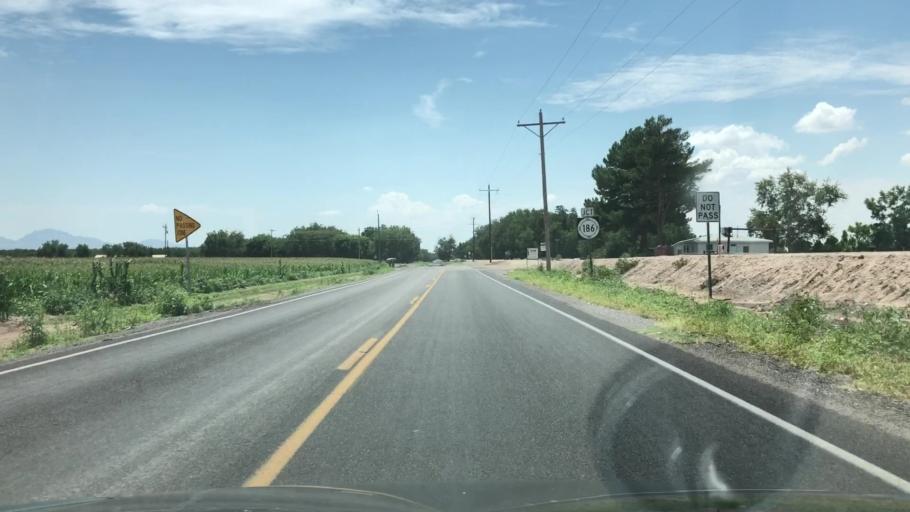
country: US
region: New Mexico
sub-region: Dona Ana County
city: Anthony
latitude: 32.0194
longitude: -106.6693
